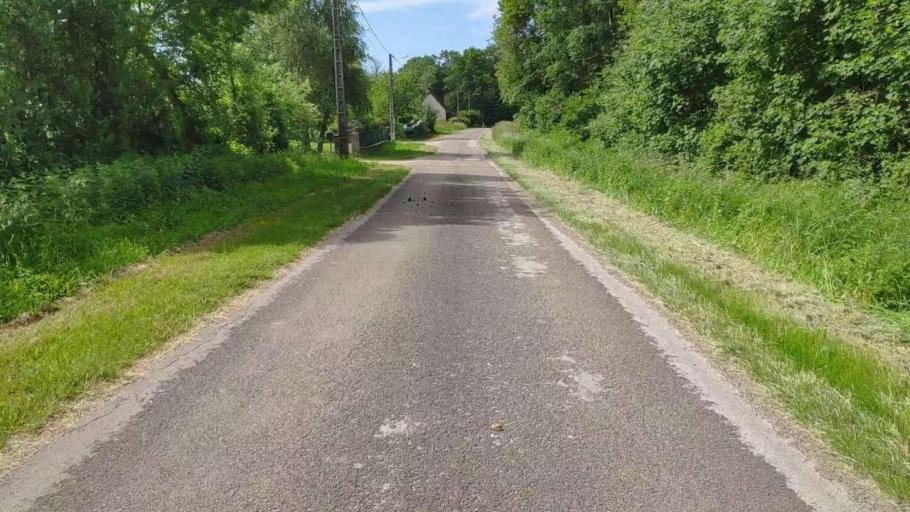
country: FR
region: Franche-Comte
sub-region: Departement du Jura
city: Bletterans
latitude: 46.7110
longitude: 5.4411
